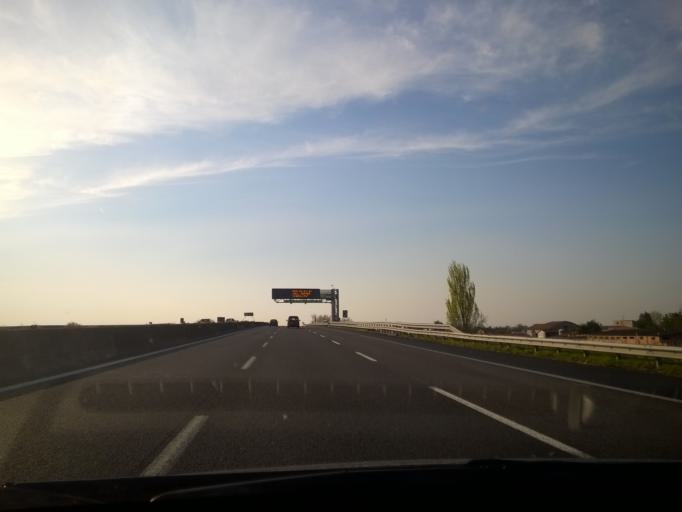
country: IT
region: Emilia-Romagna
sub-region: Provincia di Ravenna
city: Solarolo
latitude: 44.3451
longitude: 11.8416
